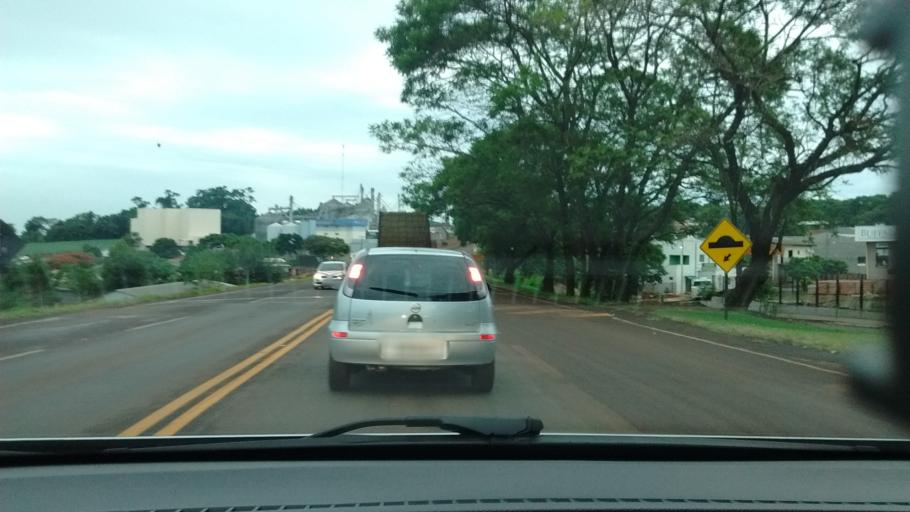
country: BR
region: Parana
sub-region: Corbelia
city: Corbelia
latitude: -24.7938
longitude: -53.2884
